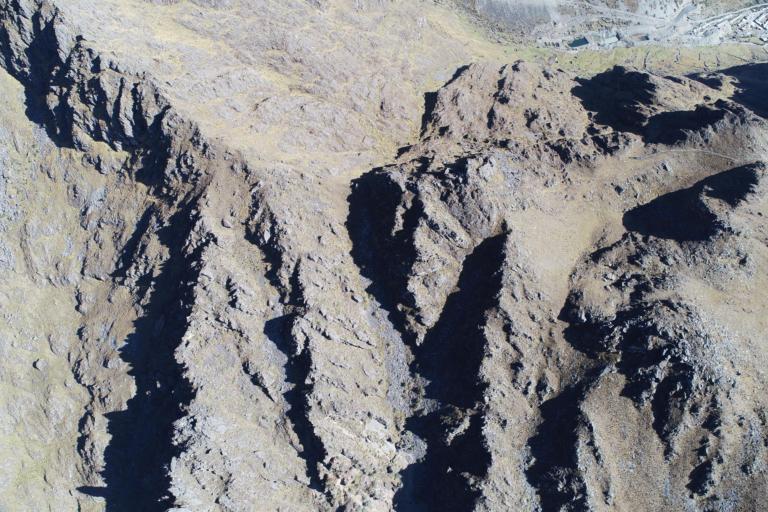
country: BO
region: La Paz
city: Sorata
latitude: -15.6557
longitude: -68.5319
